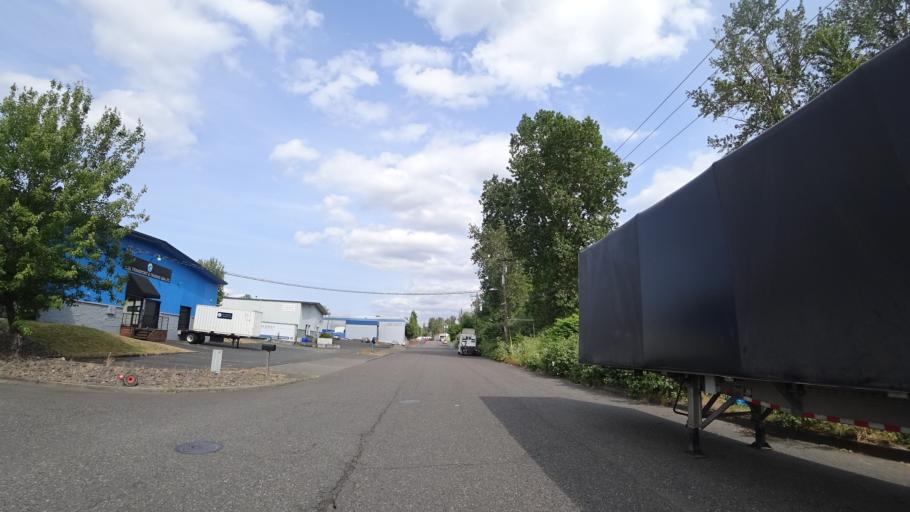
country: US
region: Oregon
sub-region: Multnomah County
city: Portland
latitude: 45.5770
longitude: -122.6399
